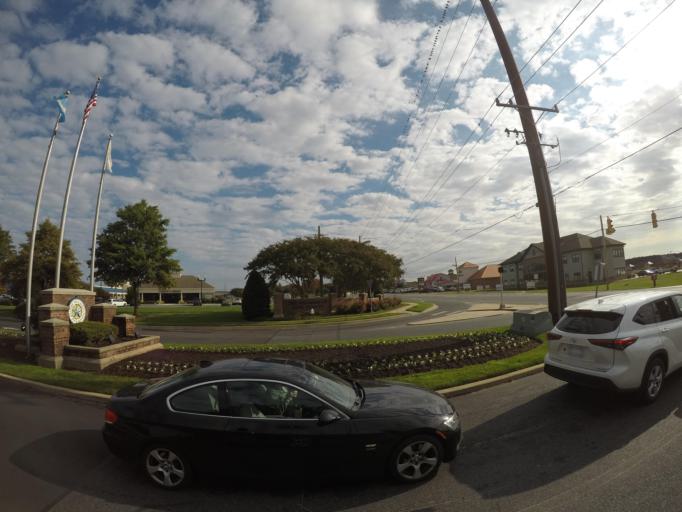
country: US
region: Delaware
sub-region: Sussex County
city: Lewes
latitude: 38.7507
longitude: -75.1679
